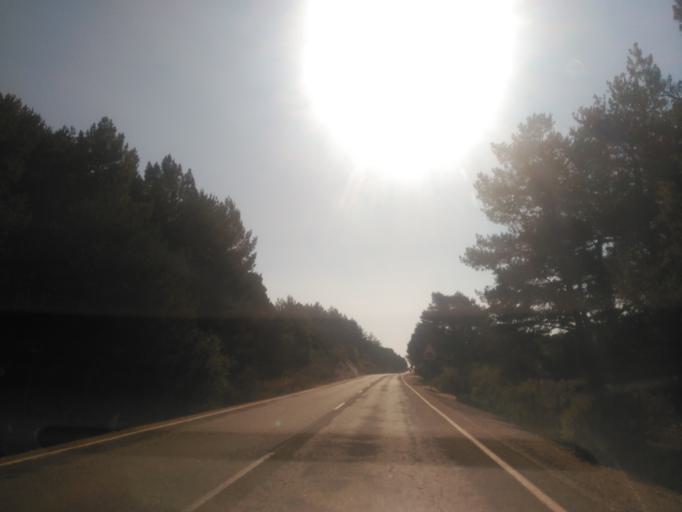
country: ES
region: Castille and Leon
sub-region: Provincia de Soria
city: San Leonardo de Yague
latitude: 41.8109
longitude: -3.0596
